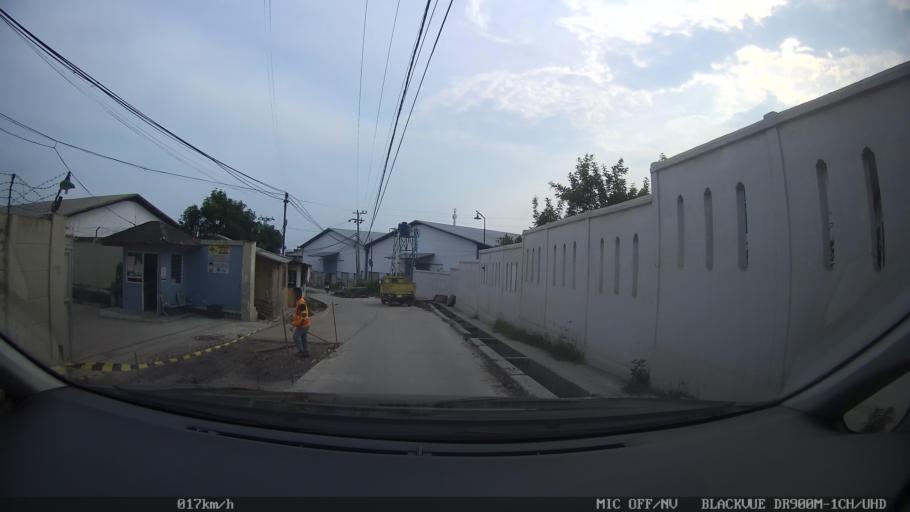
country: ID
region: Lampung
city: Panjang
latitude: -5.4387
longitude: 105.3000
